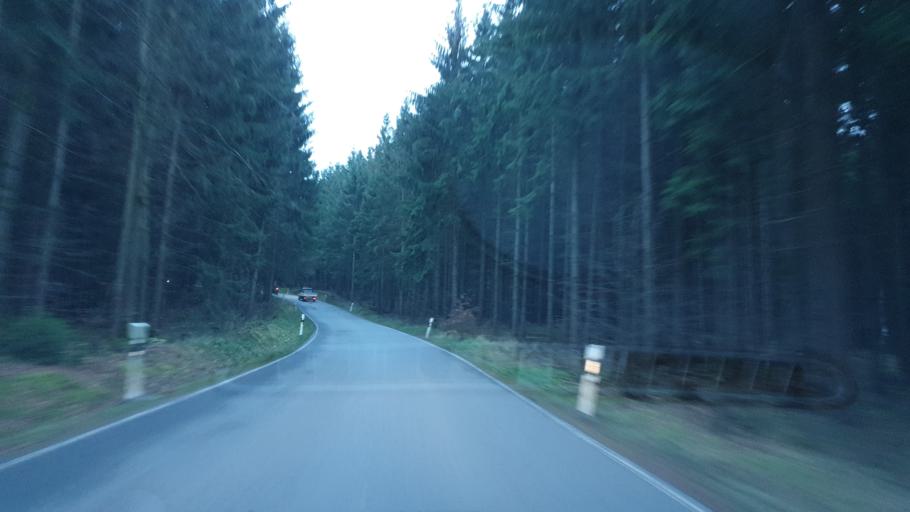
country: DE
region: Saxony
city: Hartenstein
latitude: 50.6438
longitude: 12.6526
